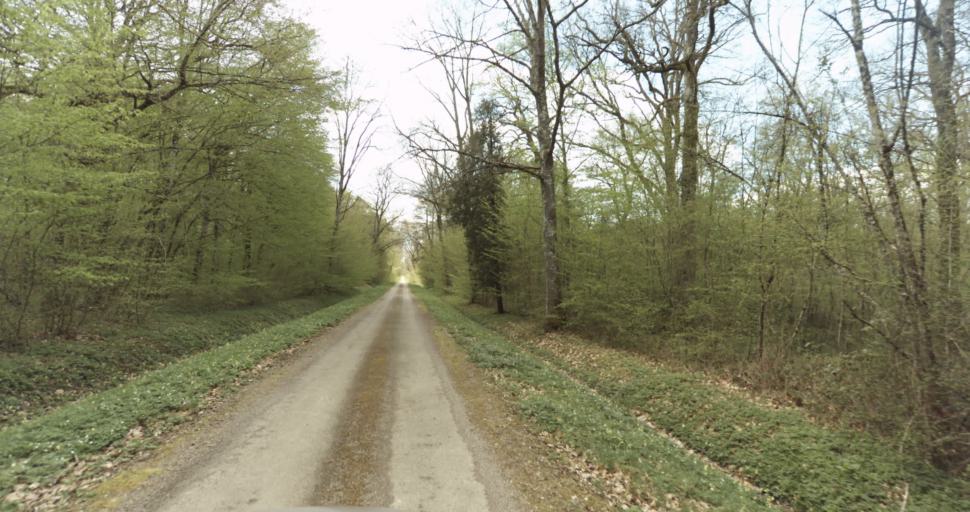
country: FR
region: Franche-Comte
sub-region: Departement du Jura
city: Champvans
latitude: 47.1623
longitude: 5.4422
